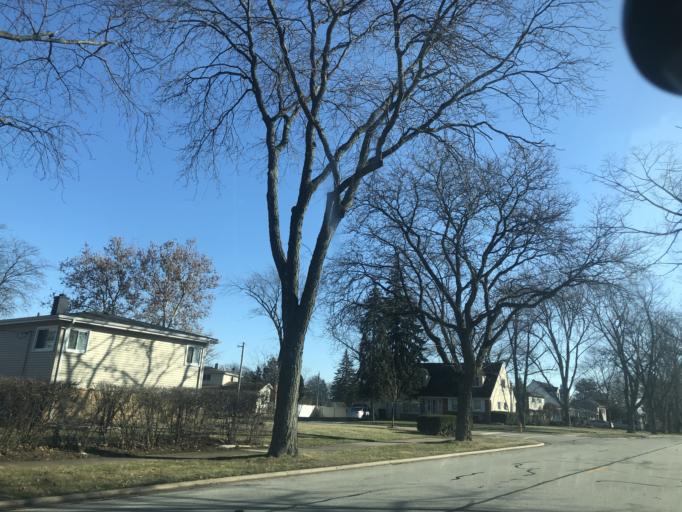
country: US
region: Illinois
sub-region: DuPage County
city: Addison
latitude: 41.9319
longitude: -88.0123
